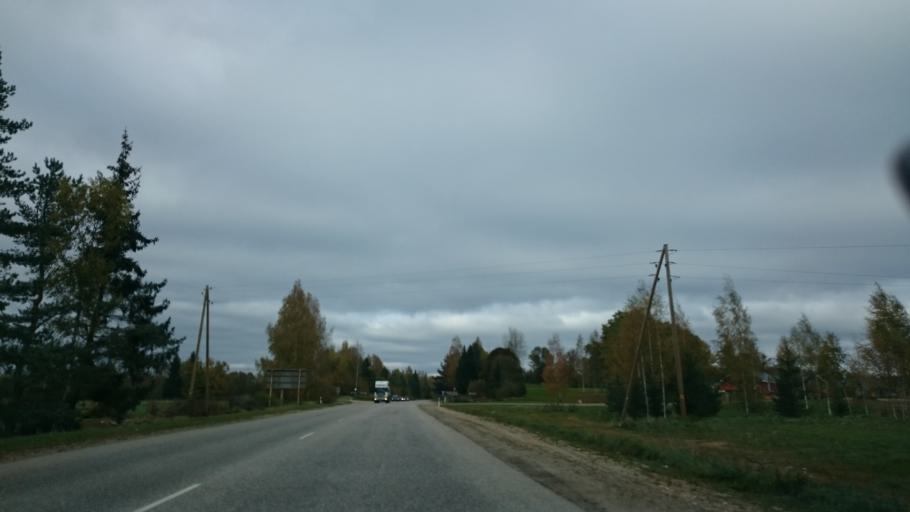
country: LV
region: Amatas Novads
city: Drabesi
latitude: 57.2338
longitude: 25.2535
